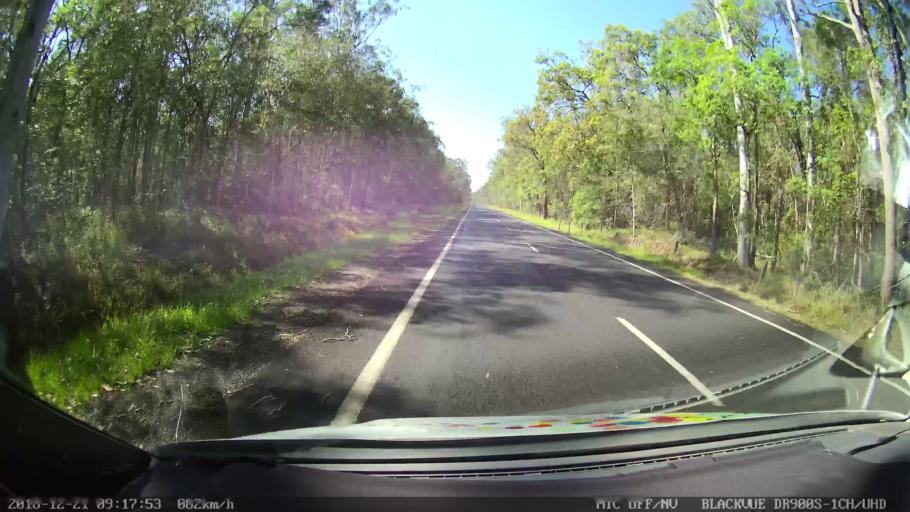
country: AU
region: New South Wales
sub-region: Clarence Valley
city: Maclean
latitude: -29.2976
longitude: 152.9921
